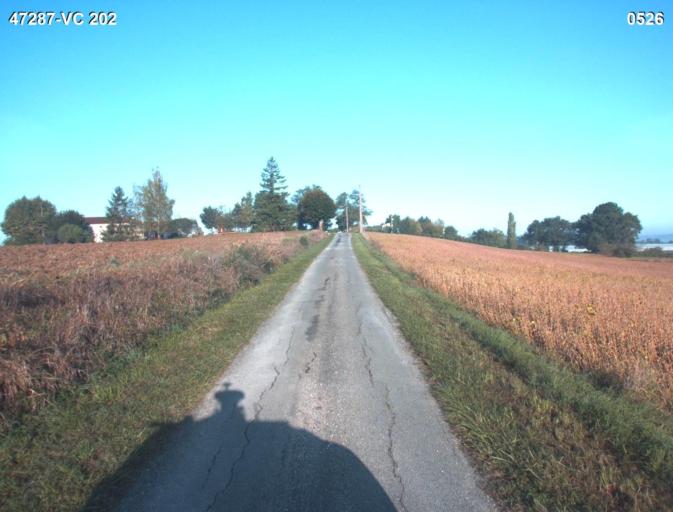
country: FR
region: Aquitaine
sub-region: Departement du Lot-et-Garonne
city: Laplume
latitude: 44.1149
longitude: 0.4650
